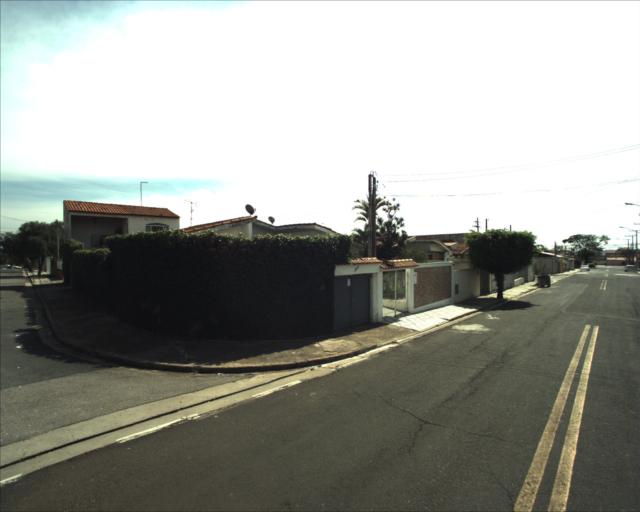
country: BR
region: Sao Paulo
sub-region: Sorocaba
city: Sorocaba
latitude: -23.5133
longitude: -47.5063
